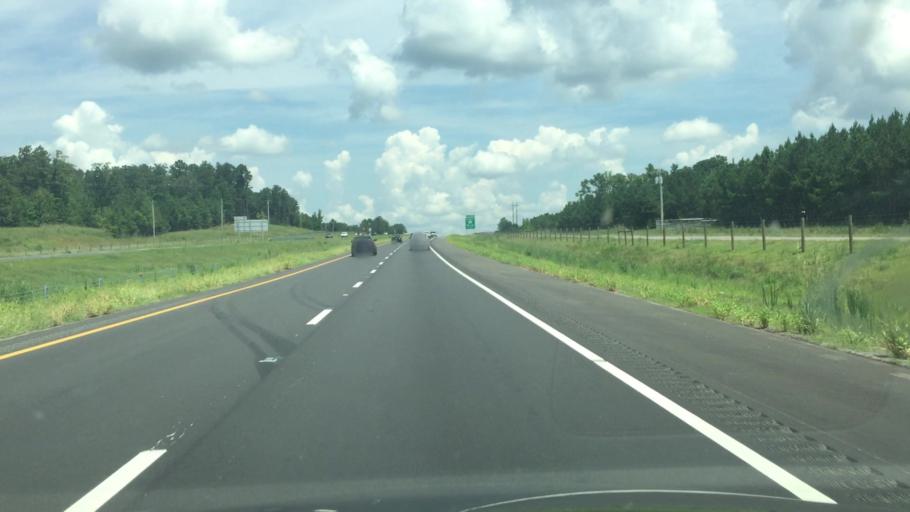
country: US
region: North Carolina
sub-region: Richmond County
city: Ellerbe
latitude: 35.0296
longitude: -79.7694
